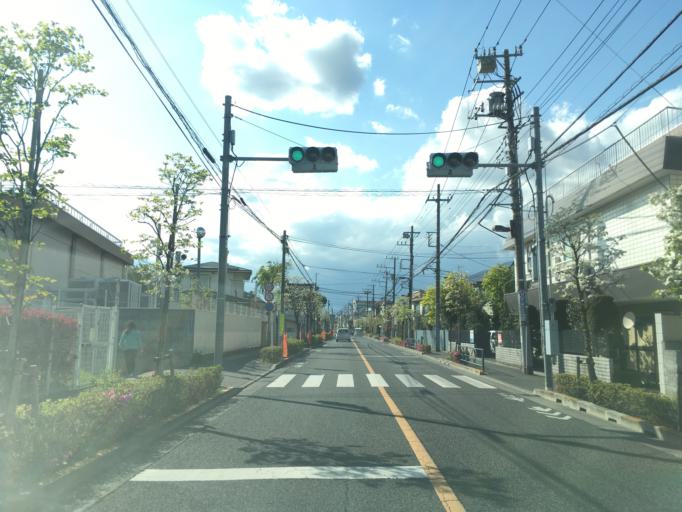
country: JP
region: Tokyo
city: Kokubunji
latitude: 35.7030
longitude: 139.4887
